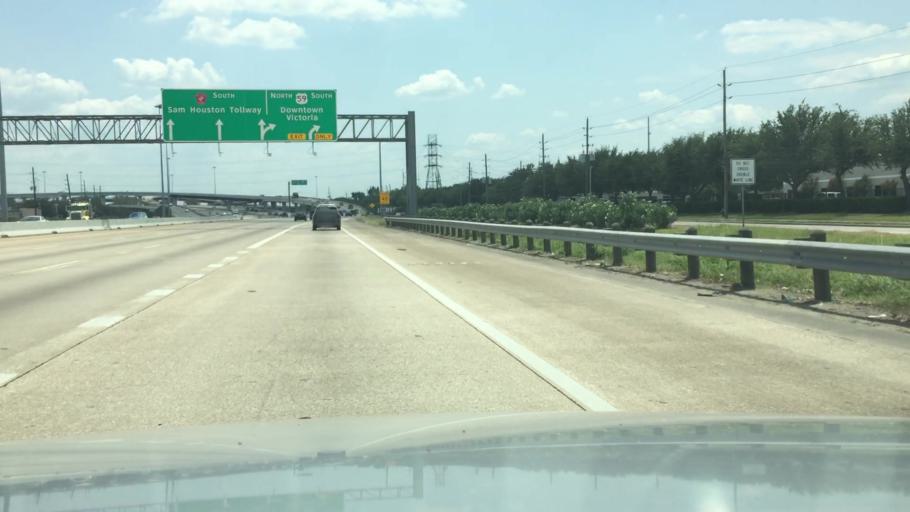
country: US
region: Texas
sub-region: Fort Bend County
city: Meadows Place
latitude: 29.6701
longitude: -95.5605
